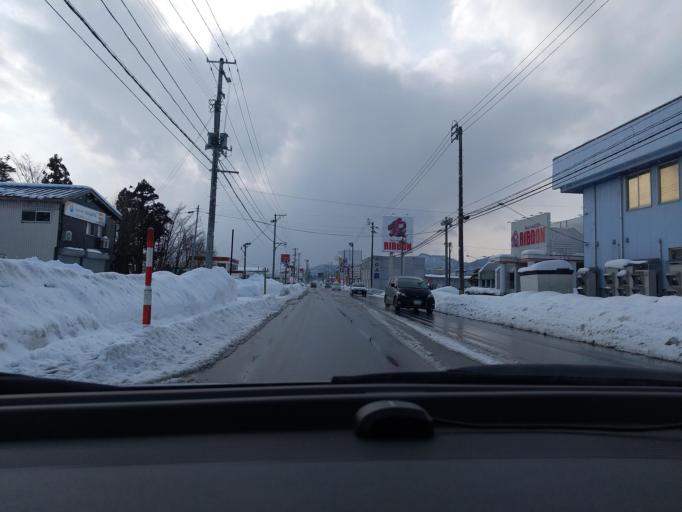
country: JP
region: Akita
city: Omagari
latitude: 39.4788
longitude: 140.4815
